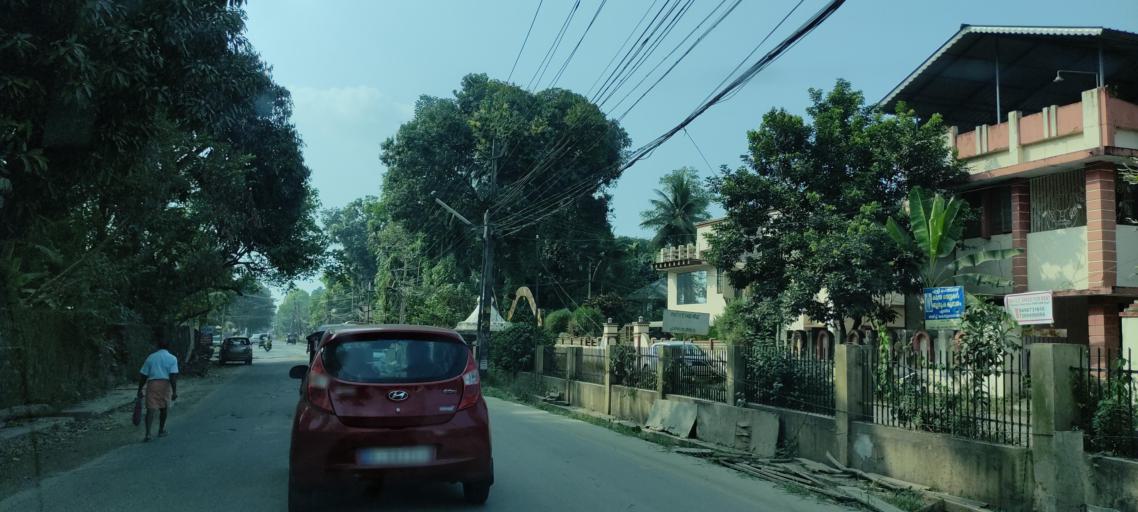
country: IN
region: Kerala
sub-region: Pattanamtitta
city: Tiruvalla
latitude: 9.3794
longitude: 76.5625
